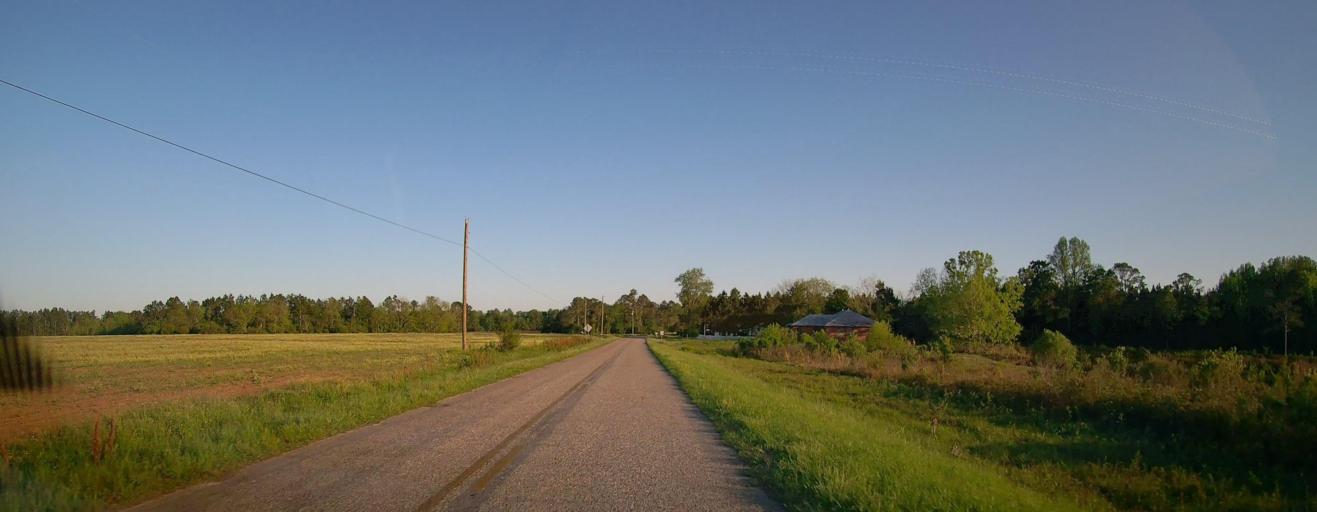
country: US
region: Georgia
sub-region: Ben Hill County
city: Fitzgerald
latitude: 31.6691
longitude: -83.2118
